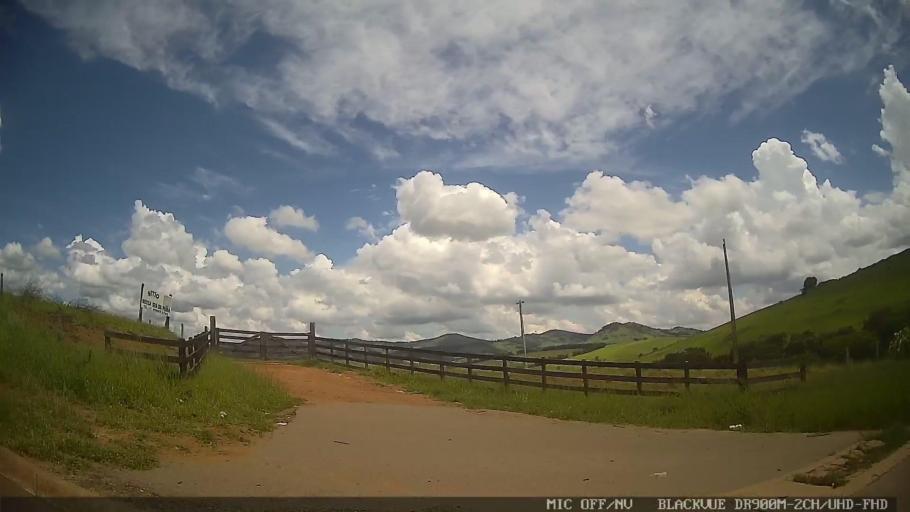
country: BR
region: Minas Gerais
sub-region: Extrema
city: Extrema
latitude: -22.7257
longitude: -46.4146
